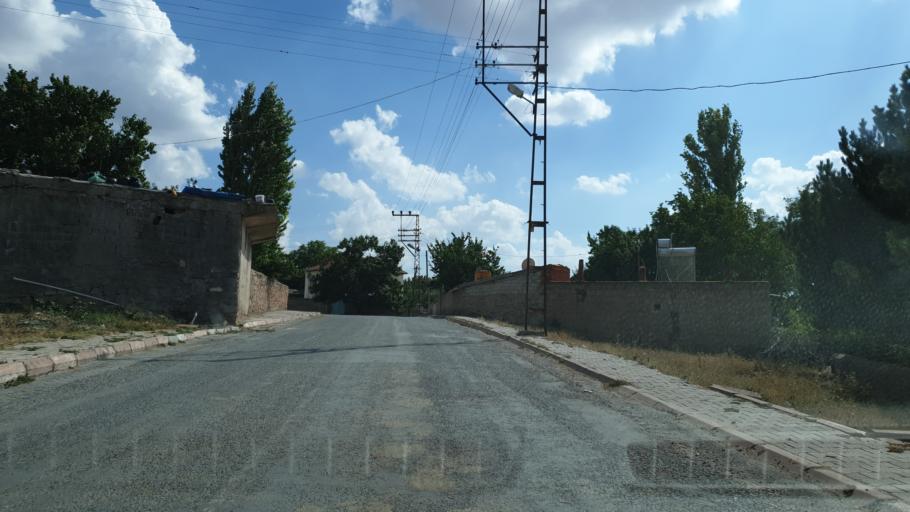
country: TR
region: Kayseri
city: Felahiye
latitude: 39.0907
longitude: 35.5630
